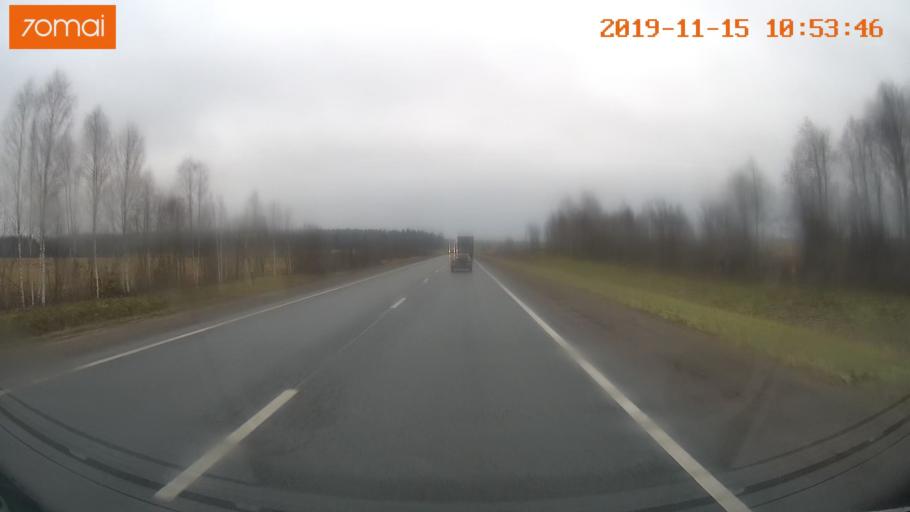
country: RU
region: Vologda
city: Chebsara
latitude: 59.1676
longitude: 38.7617
